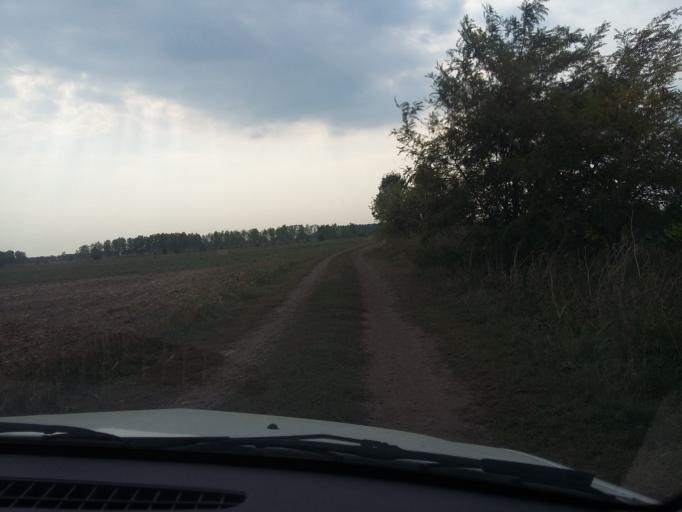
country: HU
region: Borsod-Abauj-Zemplen
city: Taktaszada
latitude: 48.1280
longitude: 21.1994
